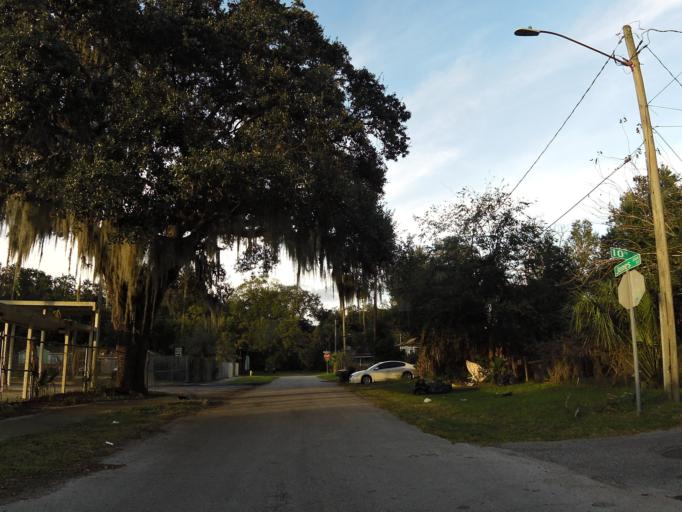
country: US
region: Florida
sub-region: Duval County
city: Jacksonville
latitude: 30.3481
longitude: -81.6340
